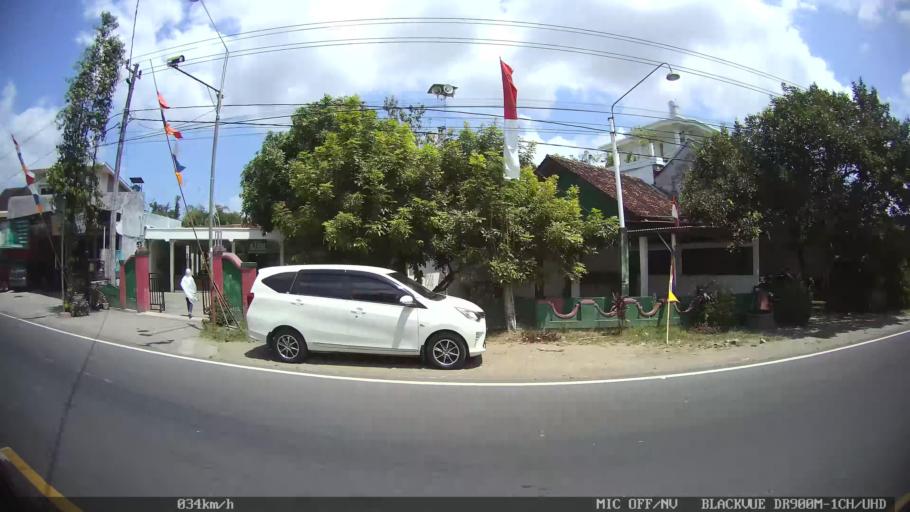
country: ID
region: Daerah Istimewa Yogyakarta
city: Bantul
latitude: -7.8821
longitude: 110.3436
